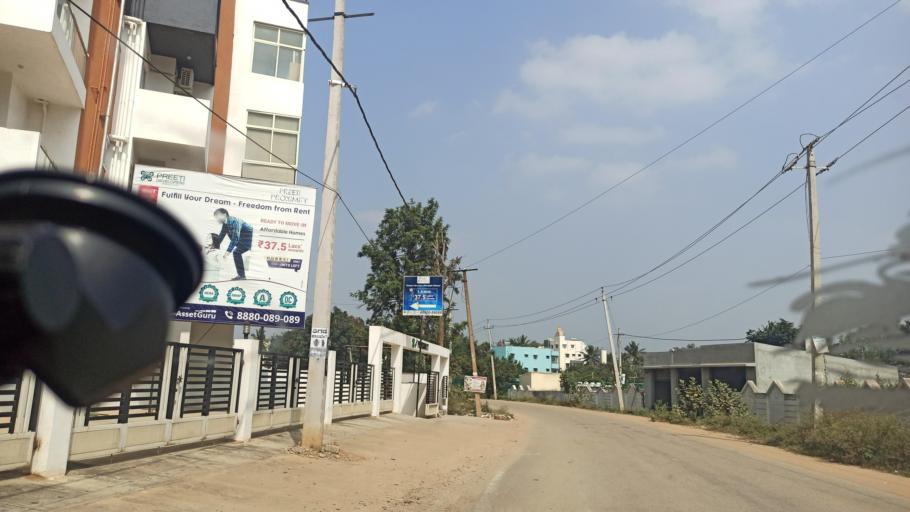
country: IN
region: Karnataka
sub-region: Bangalore Urban
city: Yelahanka
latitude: 13.0874
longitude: 77.6188
